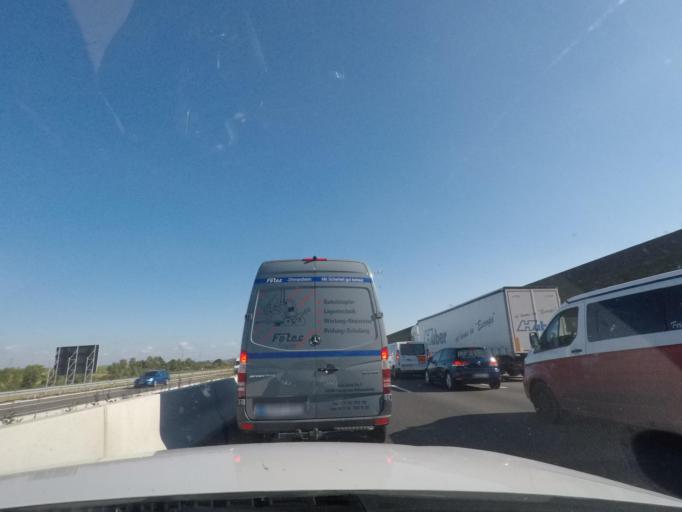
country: DE
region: Baden-Wuerttemberg
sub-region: Regierungsbezirk Stuttgart
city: Leingarten
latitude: 49.1916
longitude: 9.1123
